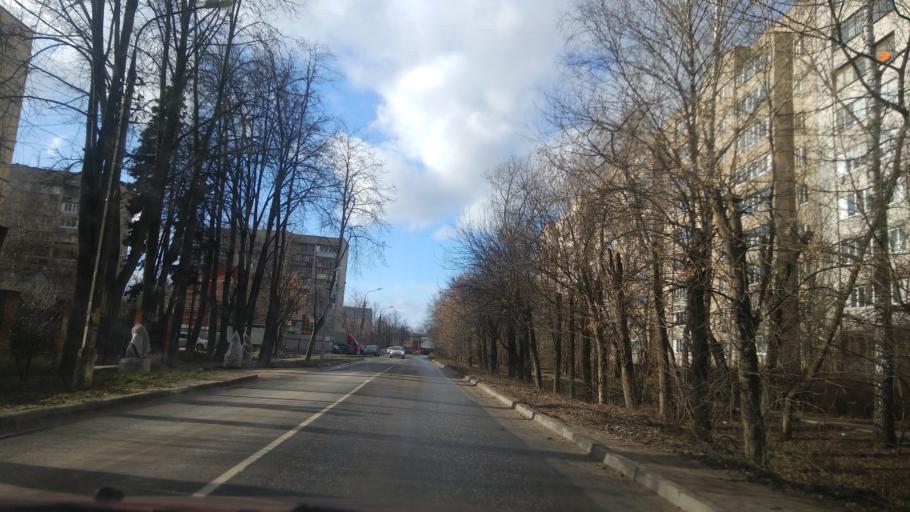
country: RU
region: Moskovskaya
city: Mamontovka
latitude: 56.0108
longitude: 37.8258
